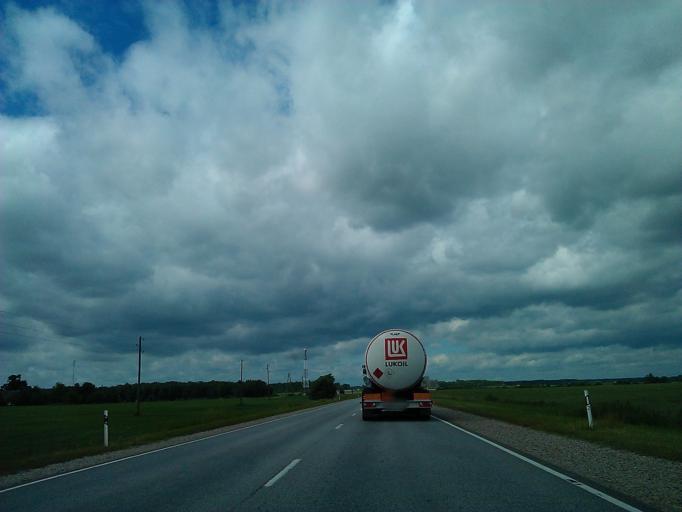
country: LV
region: Engure
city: Smarde
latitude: 56.9146
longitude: 23.3369
